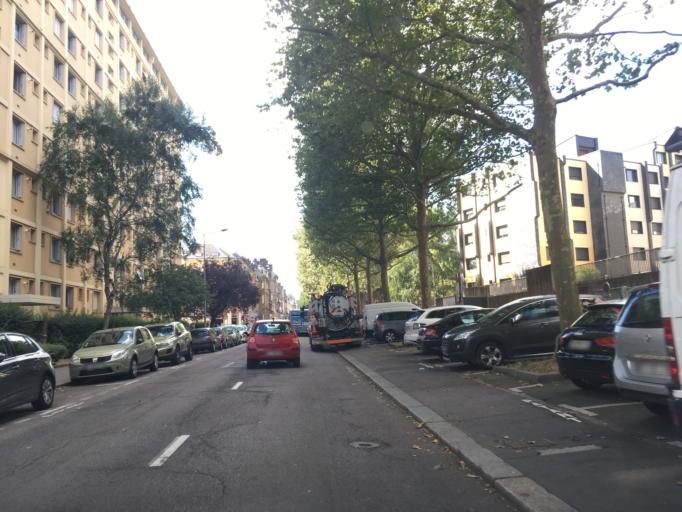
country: FR
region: Haute-Normandie
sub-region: Departement de la Seine-Maritime
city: Rouen
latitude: 49.4397
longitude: 1.1045
